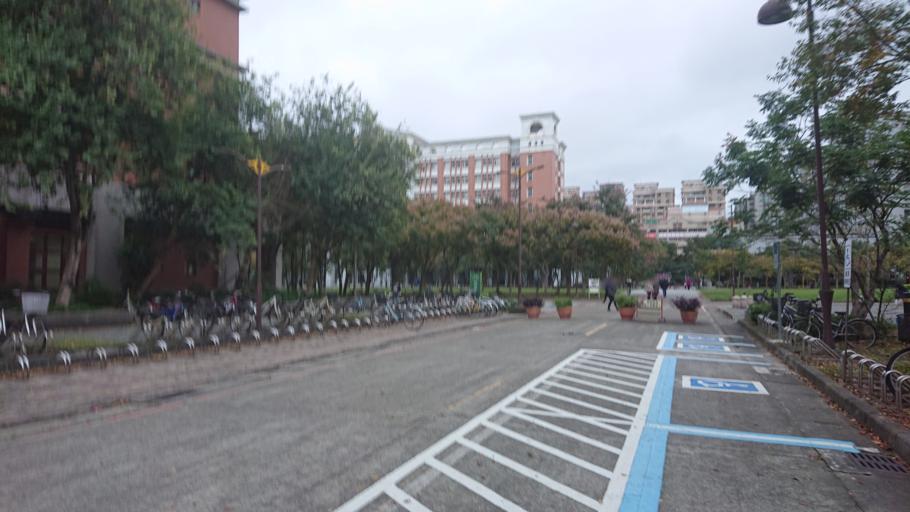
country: TW
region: Taiwan
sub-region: Taoyuan
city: Taoyuan
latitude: 24.9451
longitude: 121.3713
